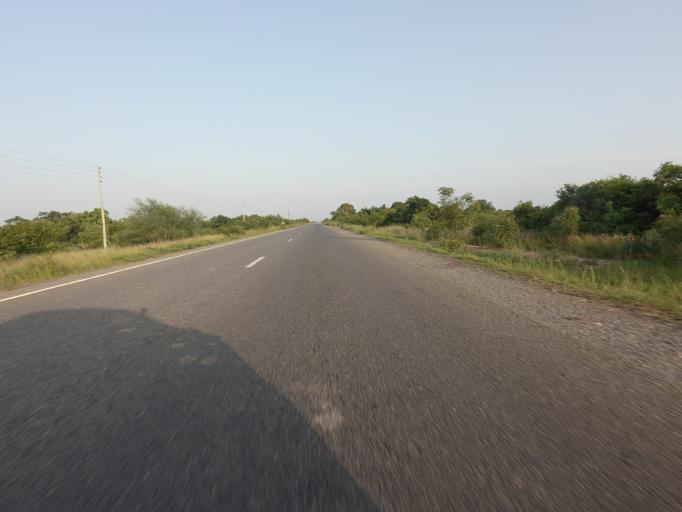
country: GH
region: Volta
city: Anloga
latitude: 5.8895
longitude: 0.7204
